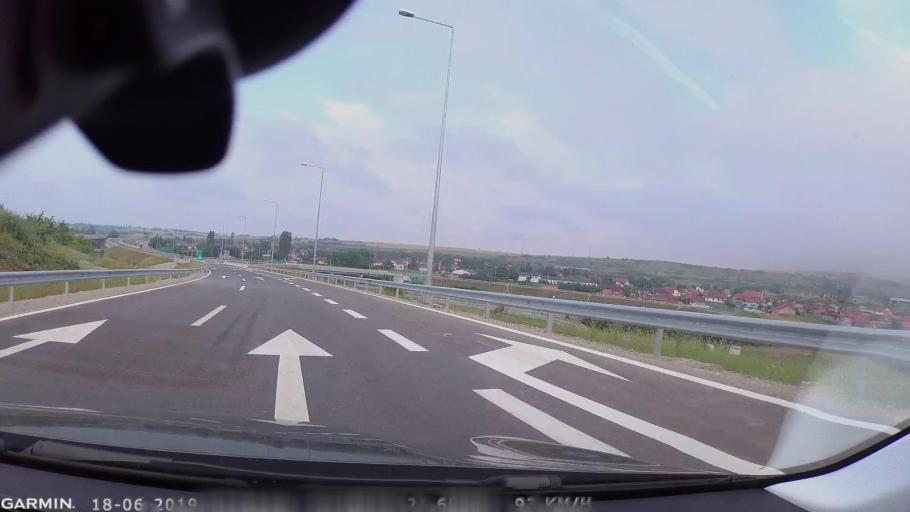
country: MK
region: Petrovec
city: Sredno Konjare
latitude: 41.9504
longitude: 21.7645
